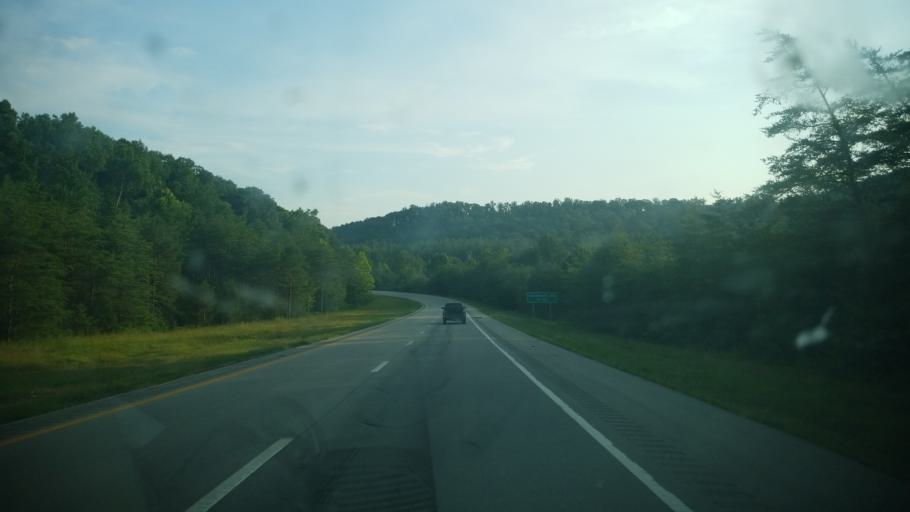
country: US
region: Ohio
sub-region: Adams County
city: Peebles
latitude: 39.0162
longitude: -83.2935
